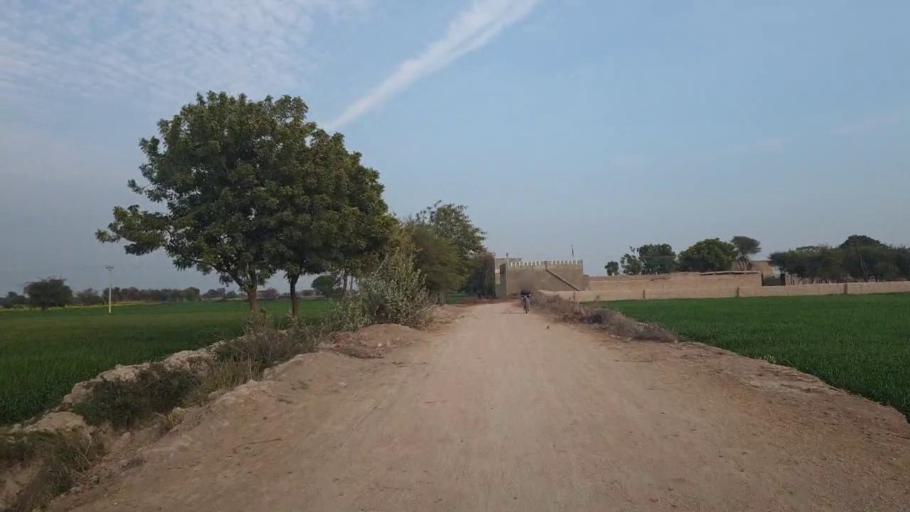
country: PK
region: Sindh
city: Shahdadpur
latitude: 26.0441
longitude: 68.5767
